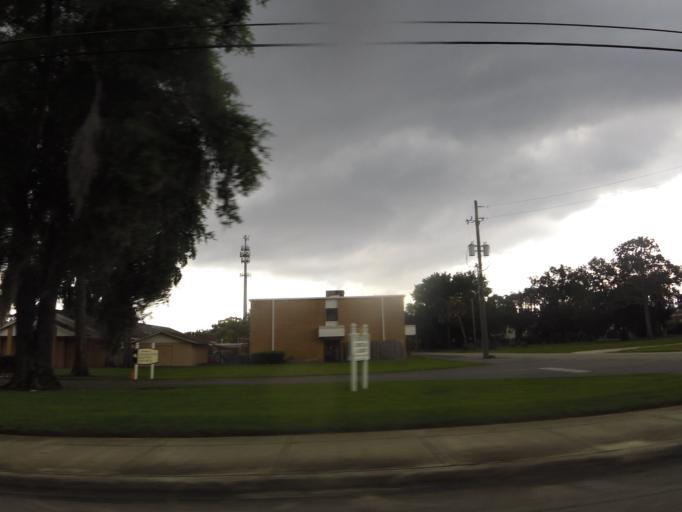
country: US
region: Florida
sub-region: Duval County
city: Jacksonville
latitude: 30.3336
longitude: -81.5956
